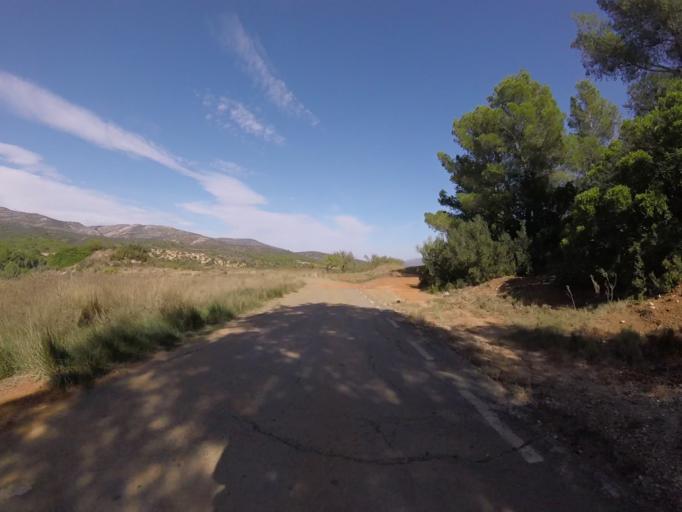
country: ES
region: Valencia
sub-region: Provincia de Castello
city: Sarratella
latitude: 40.2762
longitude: 0.0617
